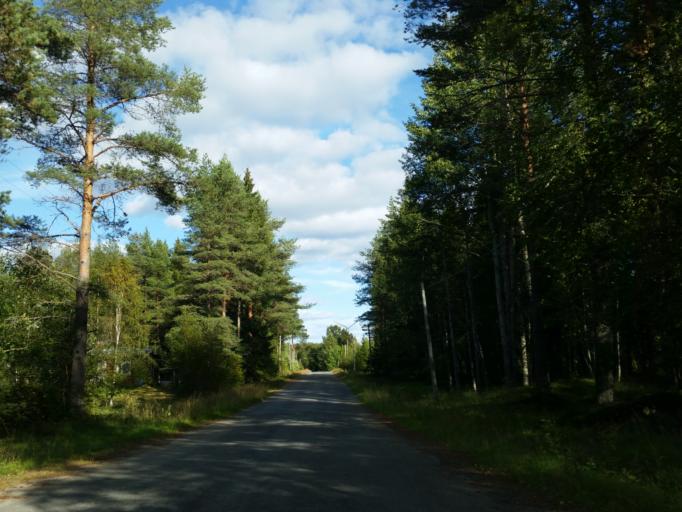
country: SE
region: Vaesterbotten
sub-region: Robertsfors Kommun
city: Robertsfors
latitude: 64.1727
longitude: 20.9507
